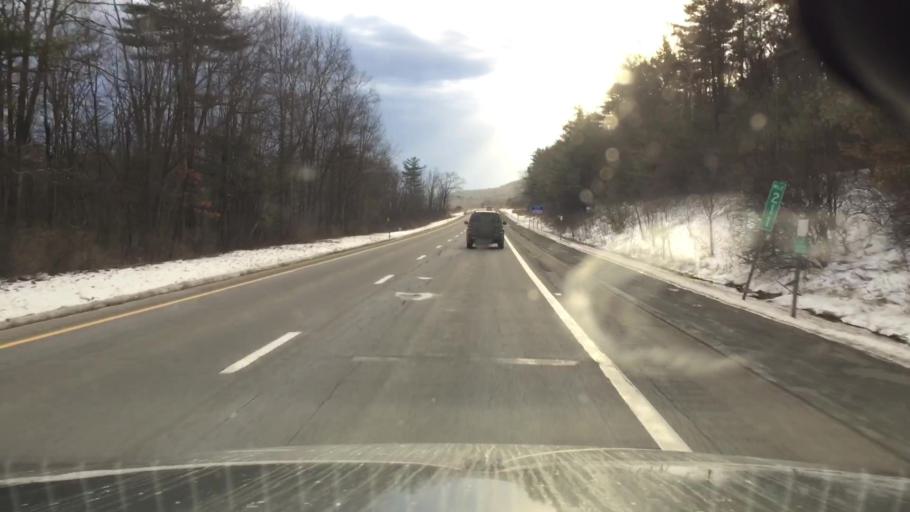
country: US
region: New York
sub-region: Tioga County
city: Waverly
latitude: 42.0273
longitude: -76.4371
